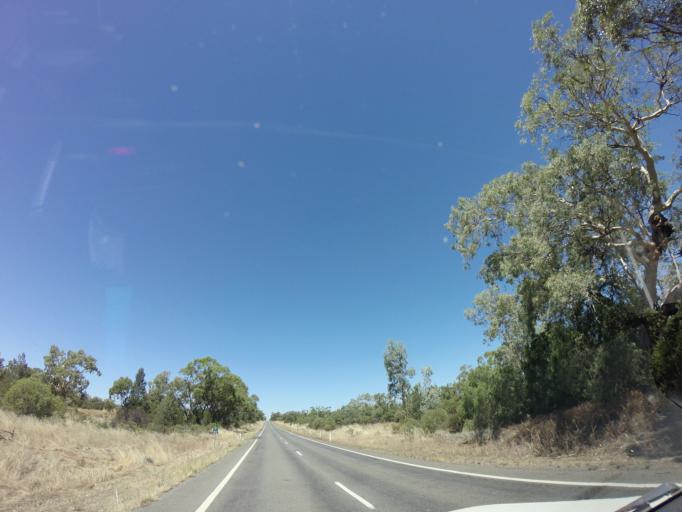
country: AU
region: New South Wales
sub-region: Bogan
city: Nyngan
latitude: -31.5504
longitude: 146.6795
